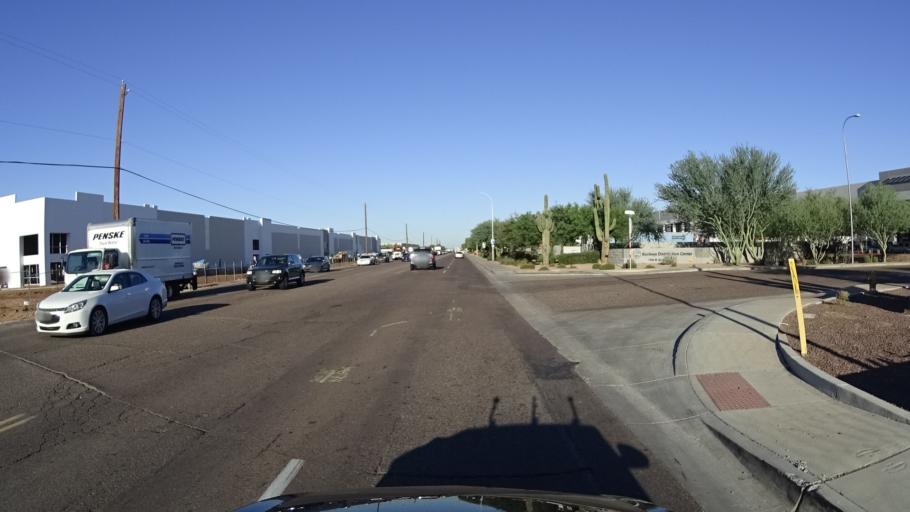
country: US
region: Arizona
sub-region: Maricopa County
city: Tolleson
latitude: 33.4373
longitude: -112.2120
